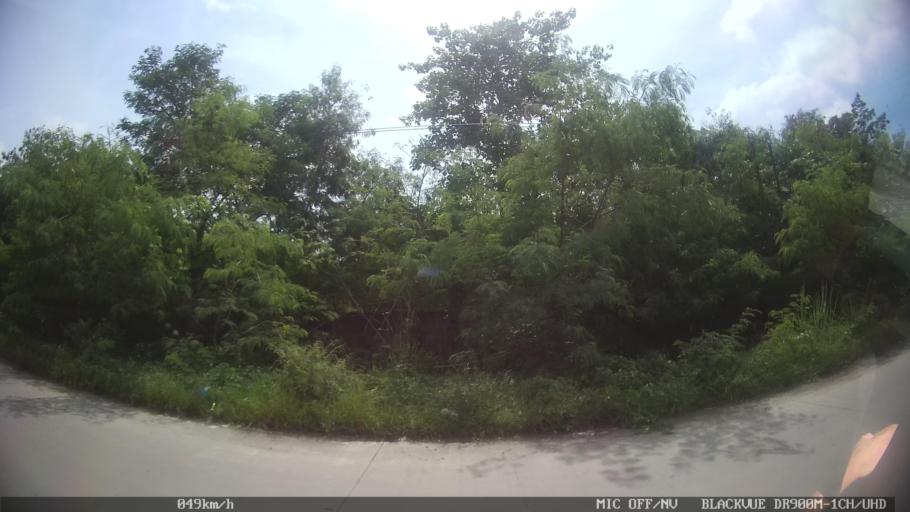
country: ID
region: North Sumatra
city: Medan
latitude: 3.6417
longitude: 98.7086
